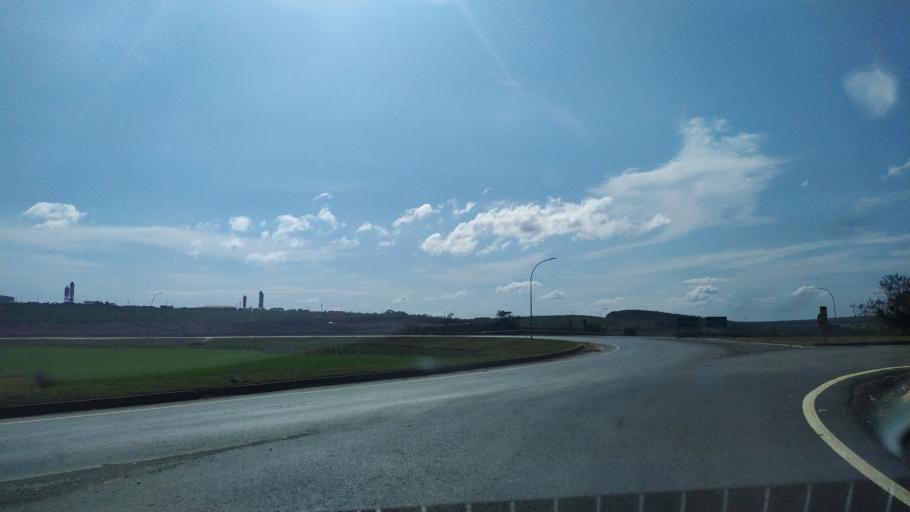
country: BR
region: Parana
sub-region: Telemaco Borba
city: Telemaco Borba
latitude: -24.2436
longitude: -50.7551
